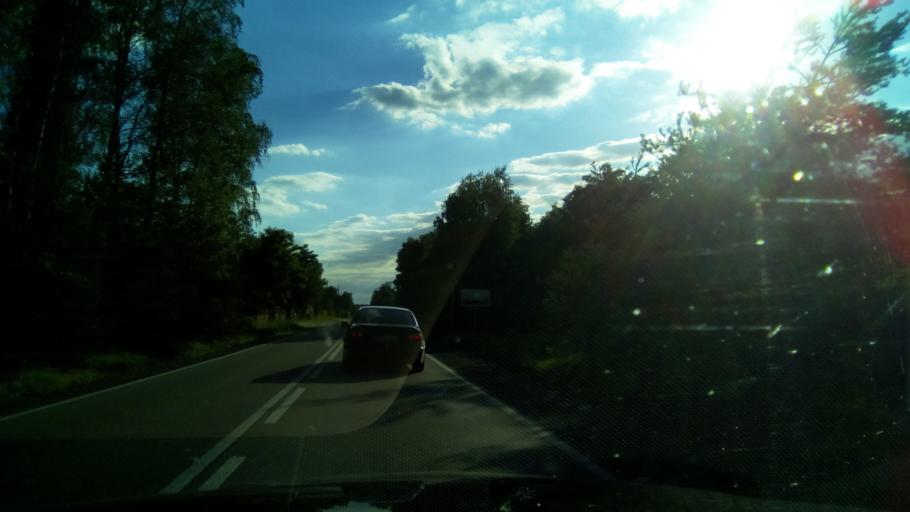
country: PL
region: Masovian Voivodeship
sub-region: Powiat bialobrzeski
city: Stromiec
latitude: 51.6484
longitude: 21.1060
